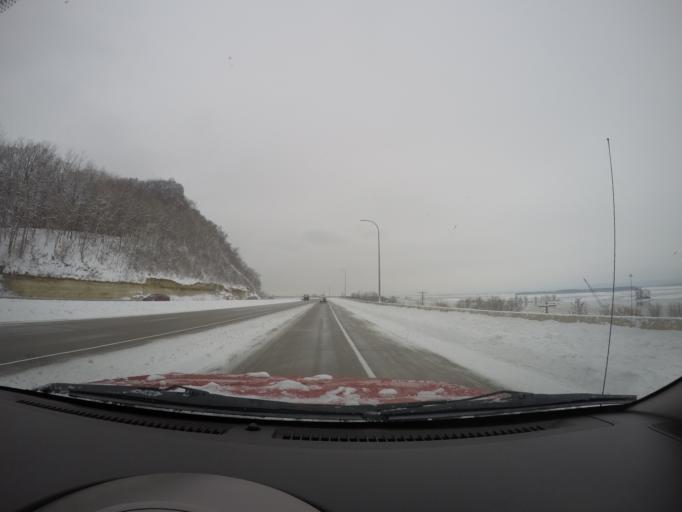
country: US
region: Minnesota
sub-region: Houston County
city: La Crescent
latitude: 43.8645
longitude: -91.3112
